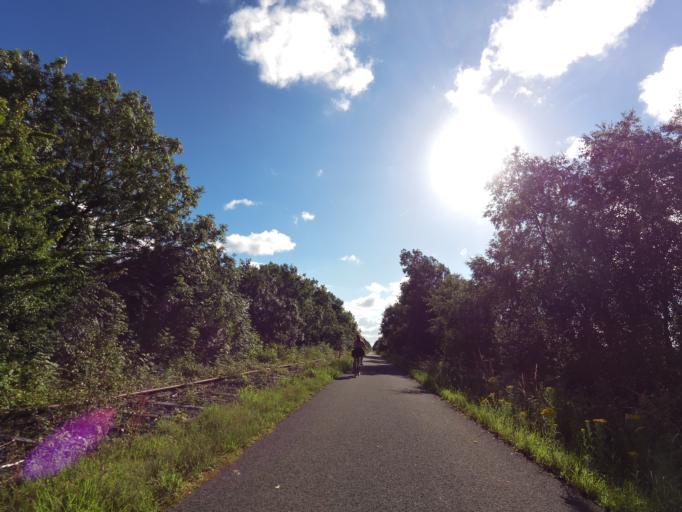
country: IE
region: Leinster
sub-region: Uibh Fhaili
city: Clara
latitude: 53.4201
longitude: -7.6252
